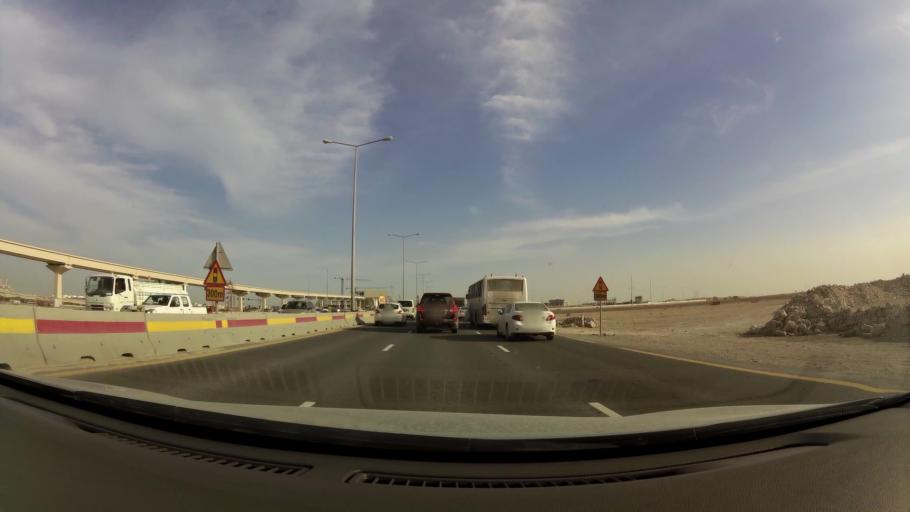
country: QA
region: Al Wakrah
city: Al Wakrah
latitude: 25.1985
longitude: 51.5923
